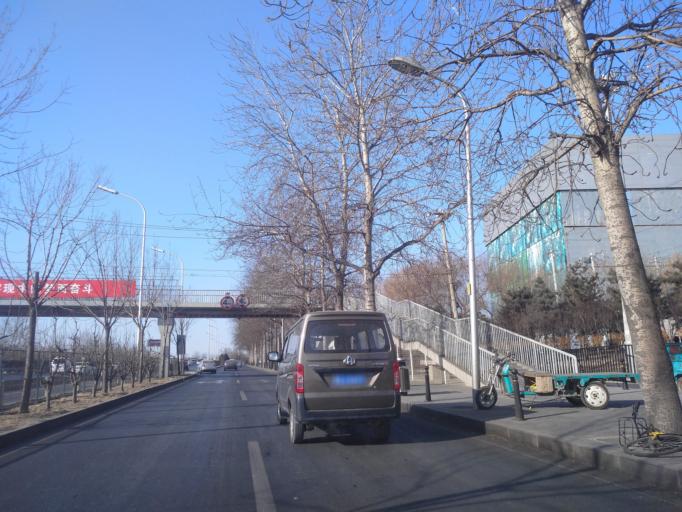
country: CN
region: Beijing
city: Jiugong
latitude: 39.8316
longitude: 116.4480
